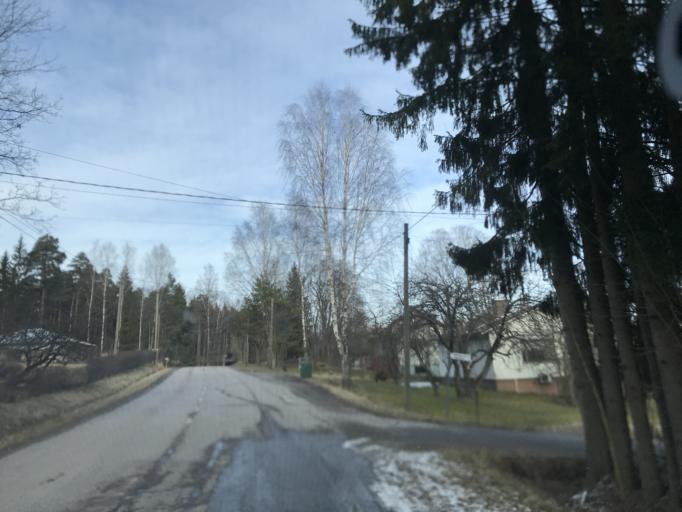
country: FI
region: Uusimaa
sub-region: Raaseporin
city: Pohja
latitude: 60.0983
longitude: 23.5396
